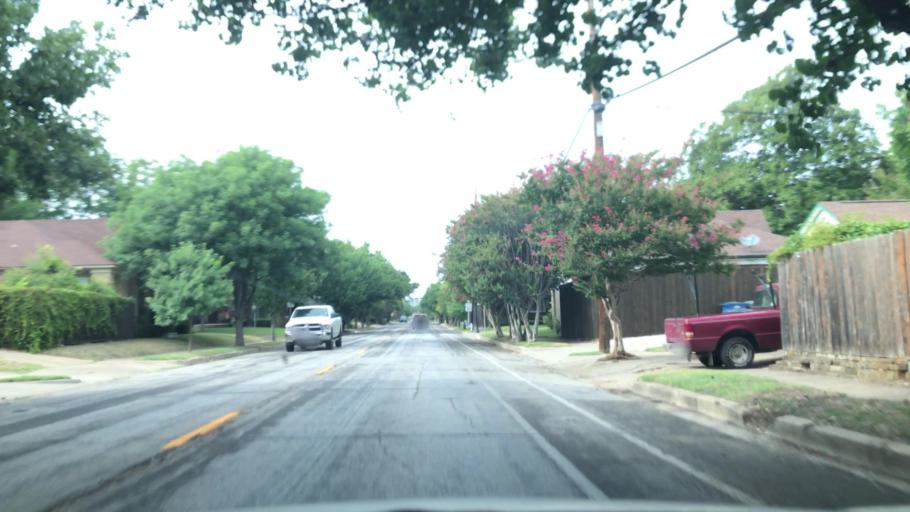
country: US
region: Texas
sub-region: Dallas County
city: Highland Park
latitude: 32.8276
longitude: -96.7747
